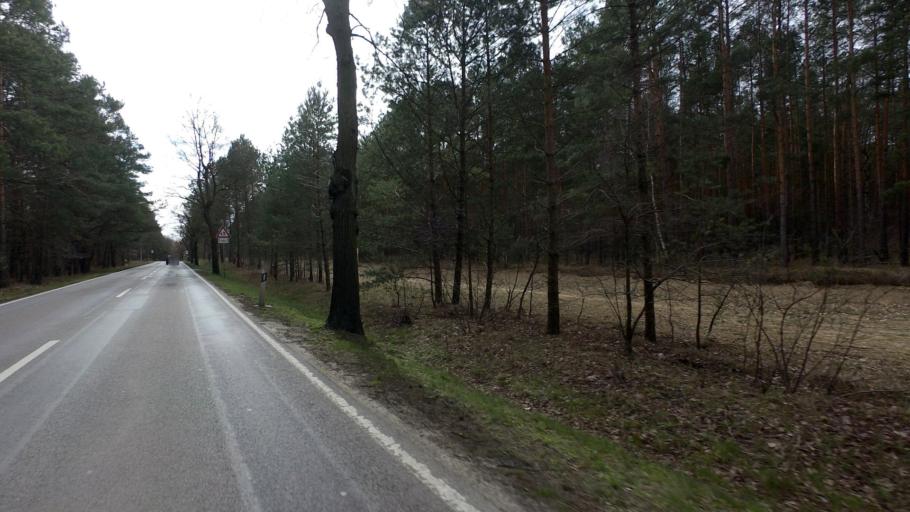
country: DE
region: Brandenburg
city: Birkenwerder
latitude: 52.7175
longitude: 13.3670
